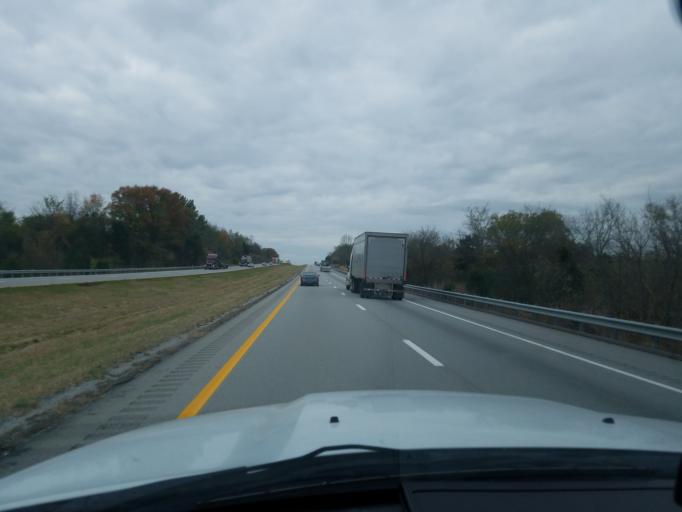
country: US
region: Kentucky
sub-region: Trimble County
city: Providence
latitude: 38.5377
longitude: -85.2180
